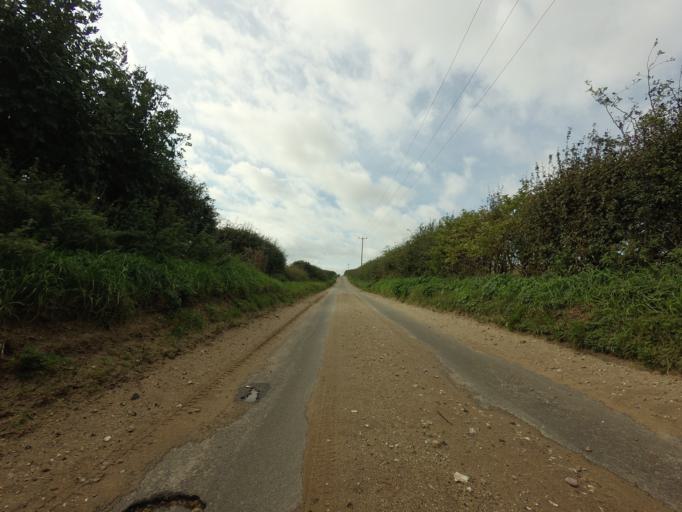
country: GB
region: England
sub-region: Norfolk
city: Hunstanton
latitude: 52.9379
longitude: 0.6750
